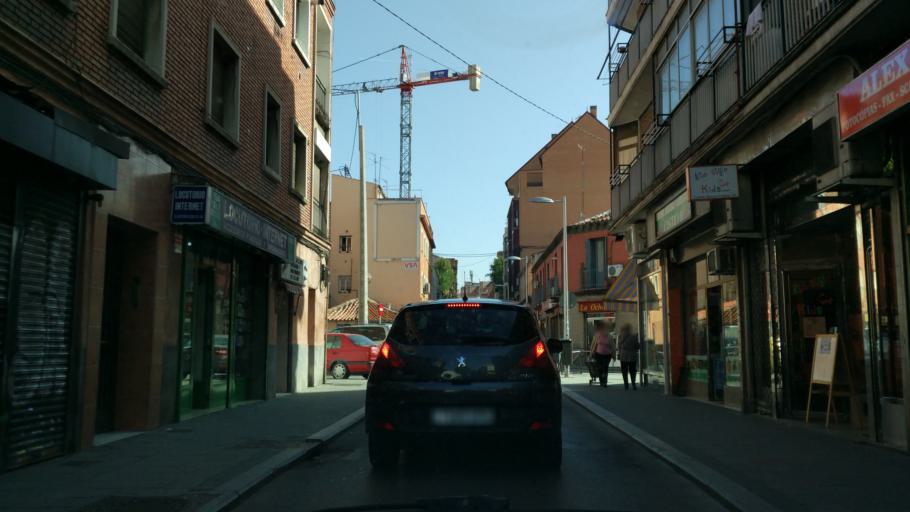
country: ES
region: Madrid
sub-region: Provincia de Madrid
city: Tetuan de las Victorias
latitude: 40.4657
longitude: -3.6998
